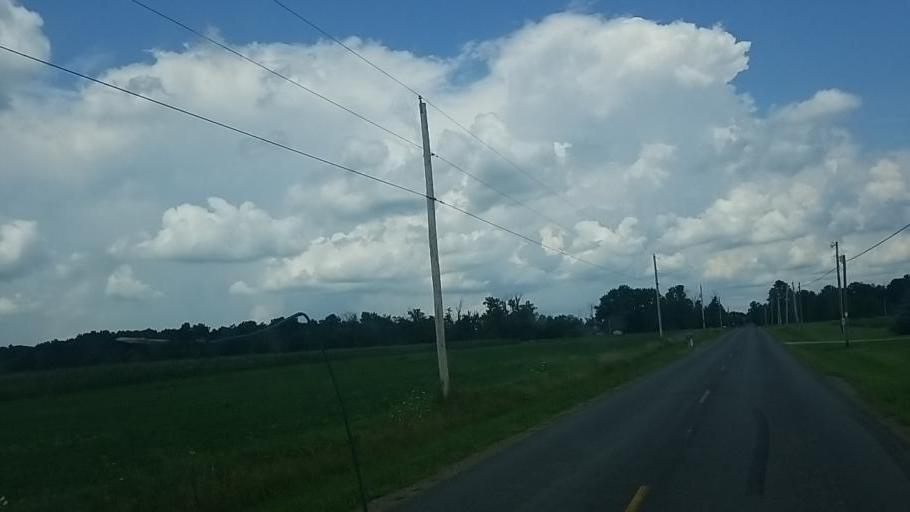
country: US
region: Ohio
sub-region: Medina County
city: Lodi
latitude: 41.0711
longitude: -82.0763
